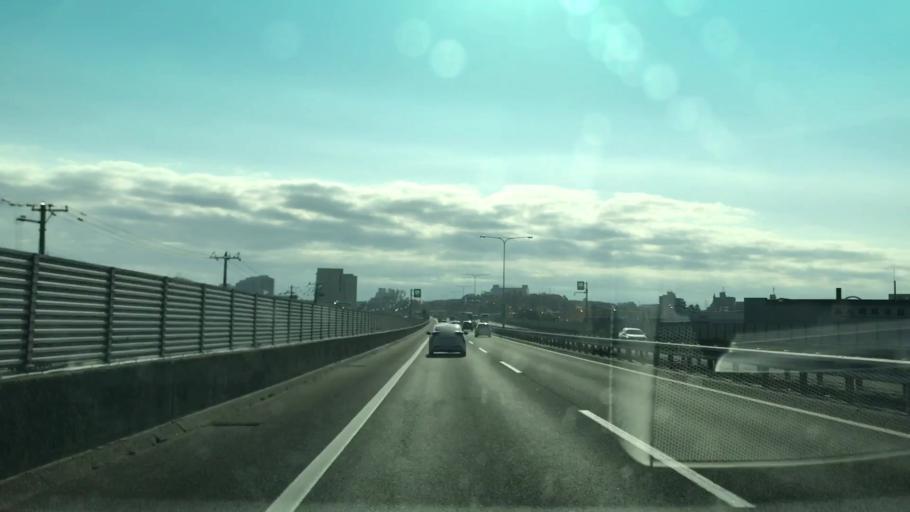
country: JP
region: Hokkaido
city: Sapporo
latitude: 43.0335
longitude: 141.4437
